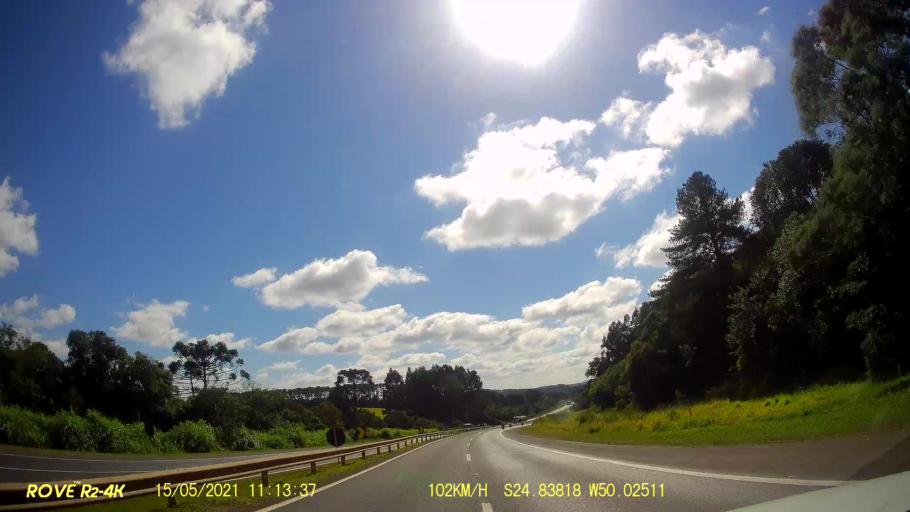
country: BR
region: Parana
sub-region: Castro
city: Castro
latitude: -24.8385
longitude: -50.0255
